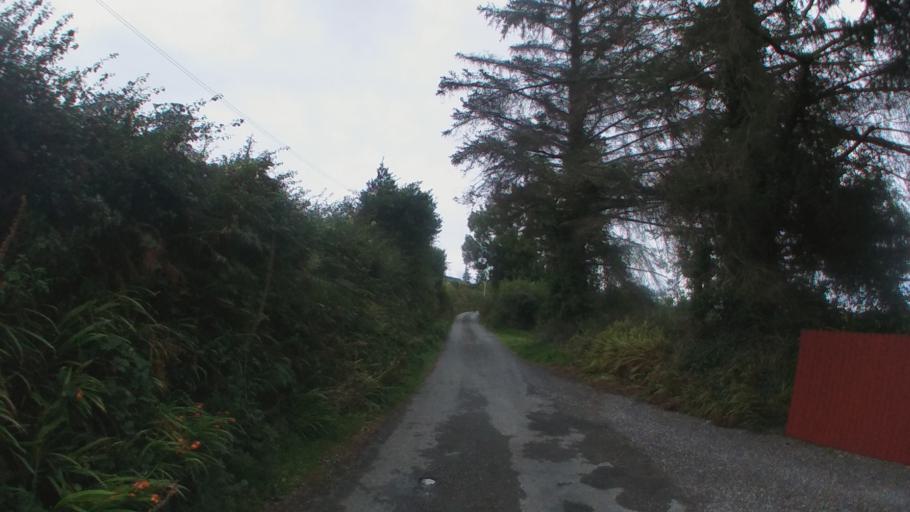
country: IE
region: Leinster
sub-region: Wicklow
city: Enniskerry
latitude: 53.1759
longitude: -6.2113
